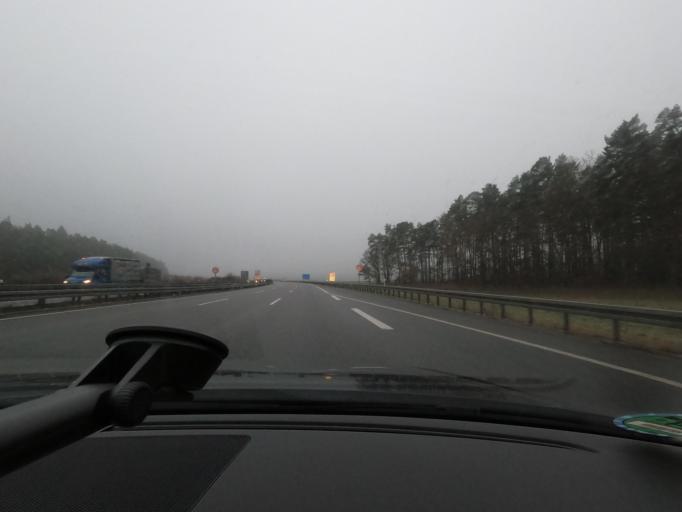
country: DE
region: Thuringia
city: Behringen
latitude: 50.7461
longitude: 10.9951
